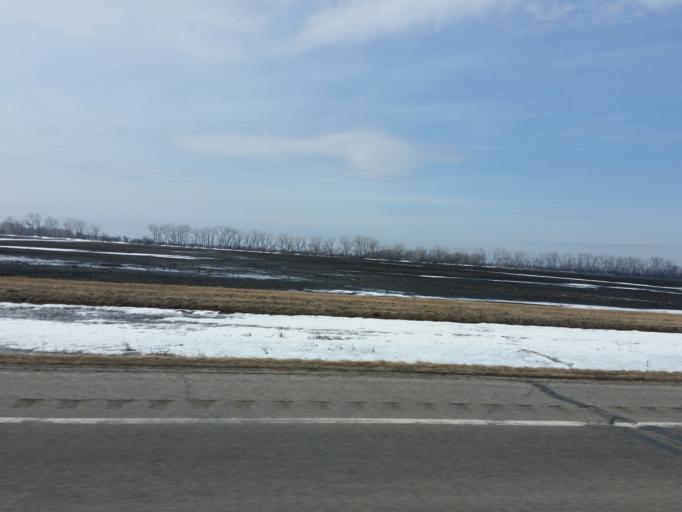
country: US
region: North Dakota
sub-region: Walsh County
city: Grafton
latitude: 48.3775
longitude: -97.4052
